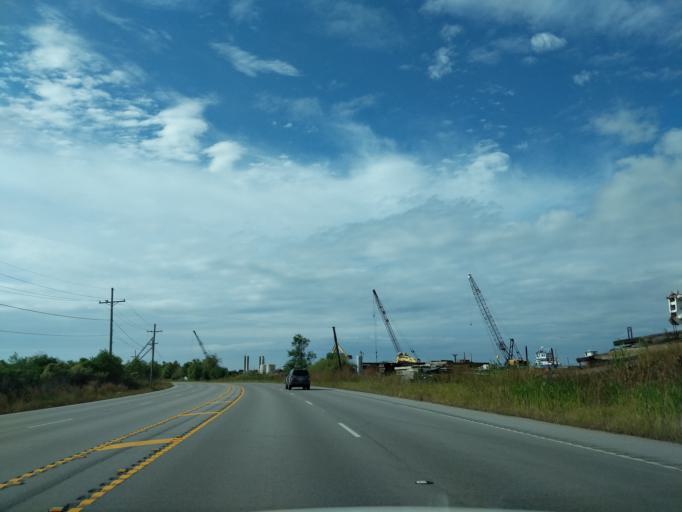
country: US
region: Louisiana
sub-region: Saint Tammany Parish
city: Eden Isle
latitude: 30.0751
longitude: -89.8423
